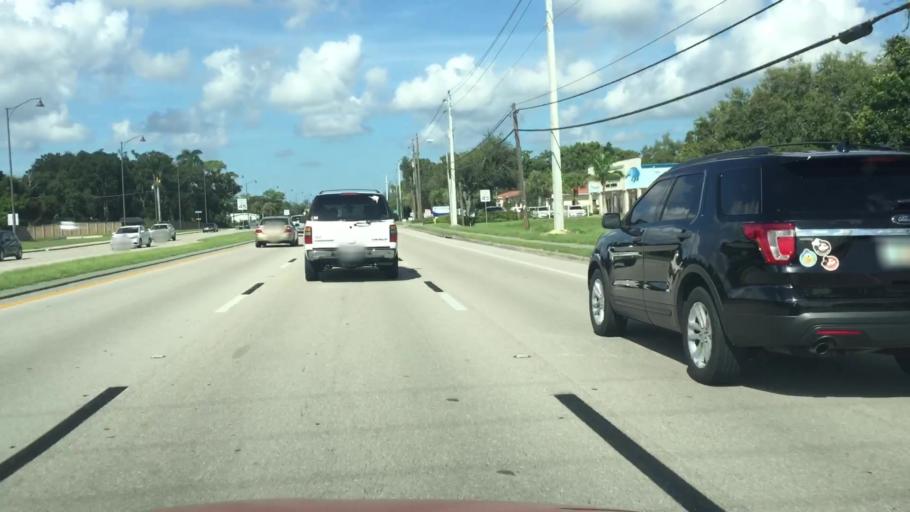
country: US
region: Florida
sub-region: Lee County
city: Bonita Springs
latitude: 26.3313
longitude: -81.7670
